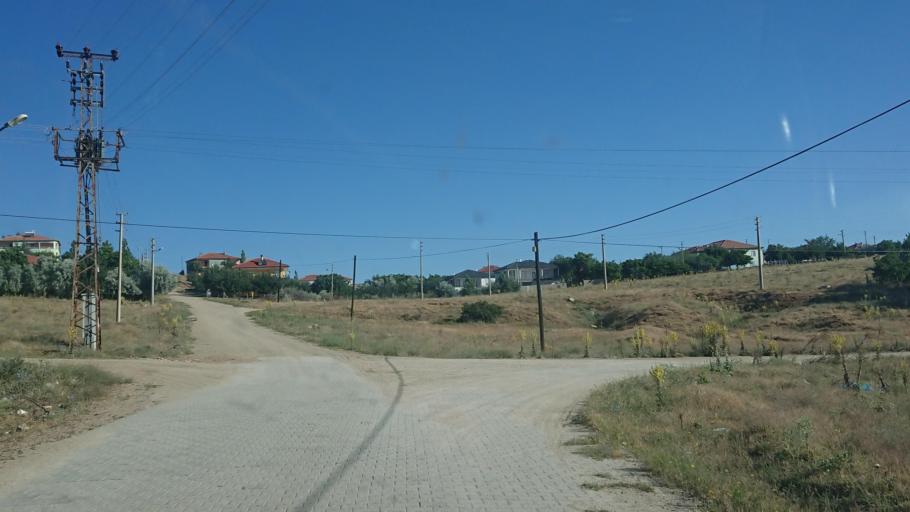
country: TR
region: Aksaray
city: Agacoren
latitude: 38.8717
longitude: 33.9448
